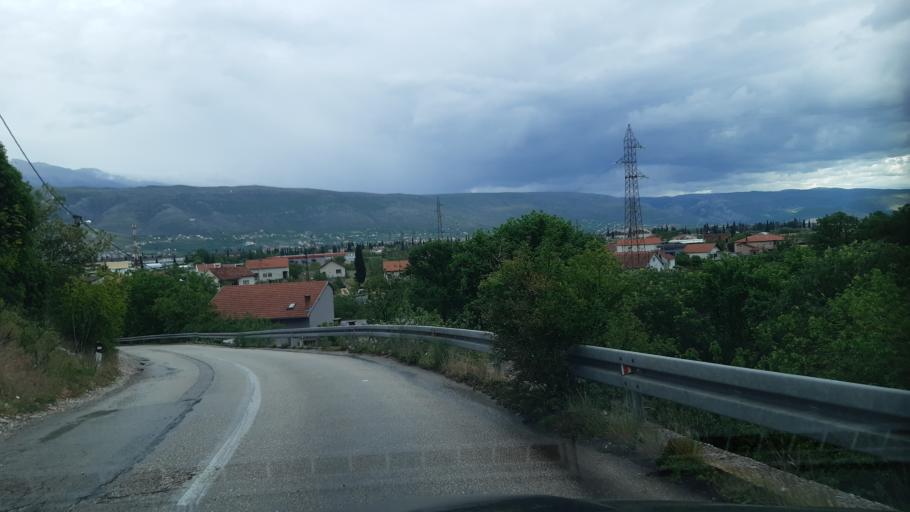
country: BA
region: Federation of Bosnia and Herzegovina
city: Rodoc
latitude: 43.3047
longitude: 17.7955
